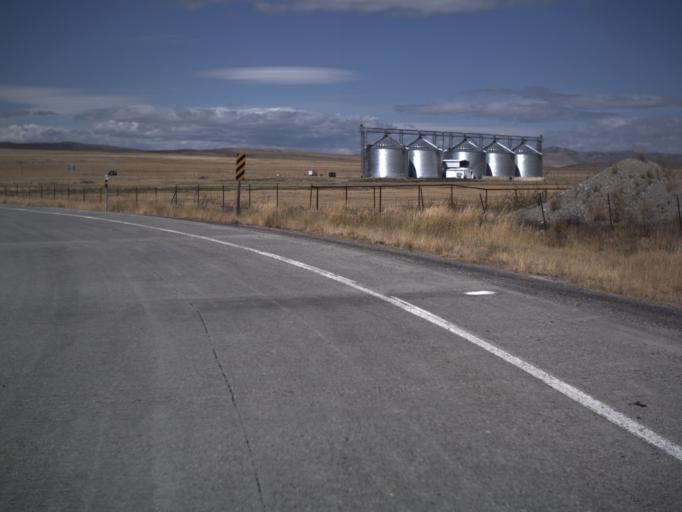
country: US
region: Utah
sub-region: Box Elder County
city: Garland
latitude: 41.8425
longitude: -112.4361
